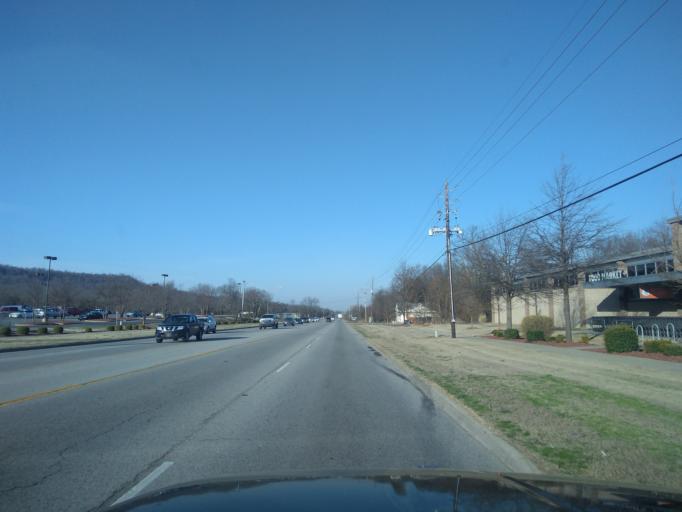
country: US
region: Arkansas
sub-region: Washington County
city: Farmington
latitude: 36.0510
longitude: -94.2060
